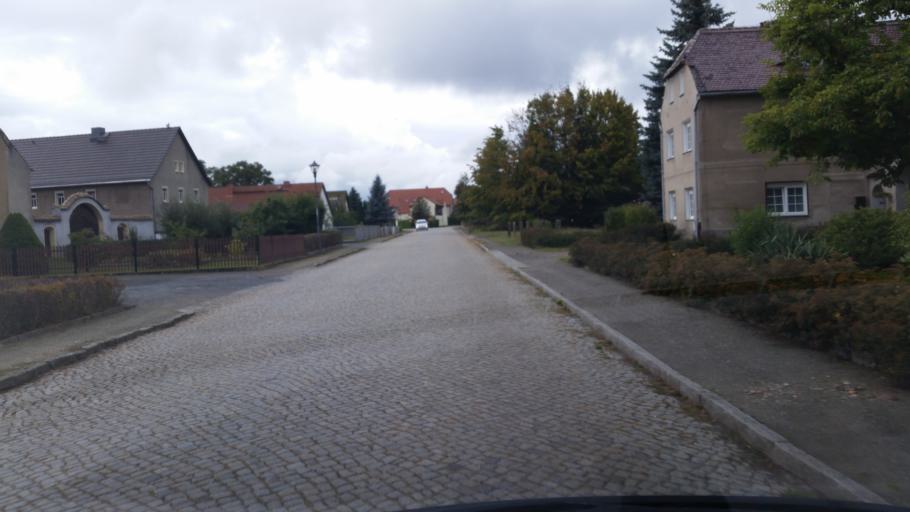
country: DE
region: Saxony
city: Ossling
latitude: 51.3136
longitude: 14.1407
